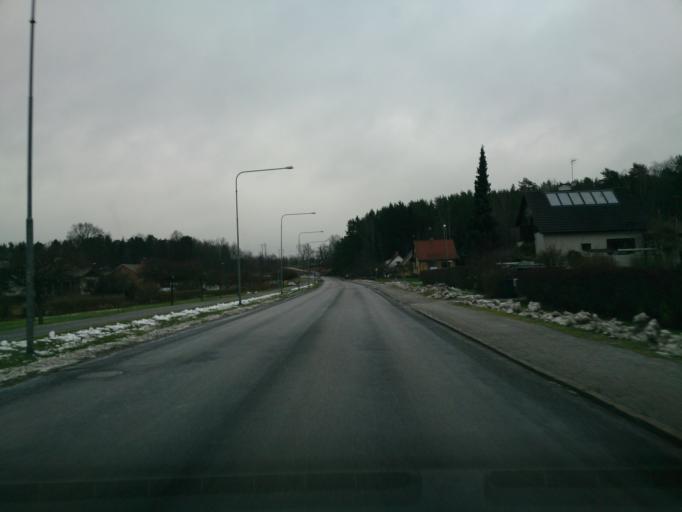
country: SE
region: OEstergoetland
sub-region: Atvidabergs Kommun
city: Atvidaberg
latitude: 58.2086
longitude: 16.0096
